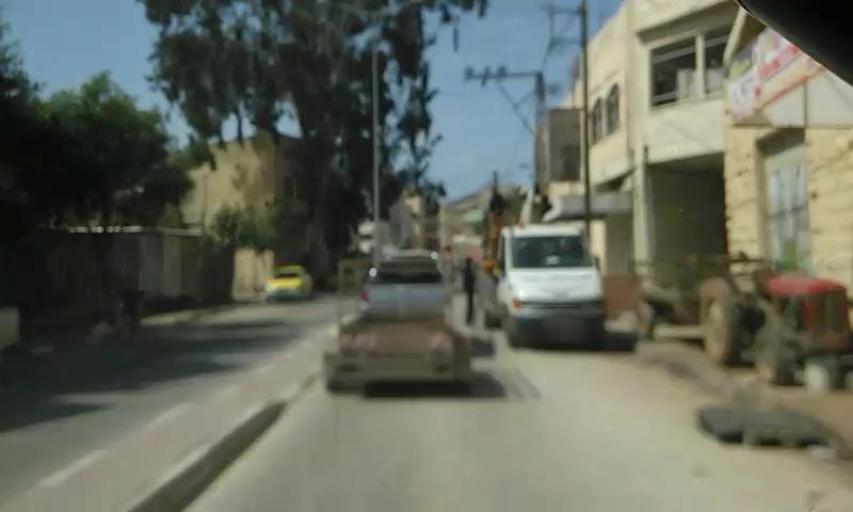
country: PS
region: West Bank
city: Qabatiyah
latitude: 32.4099
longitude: 35.2844
